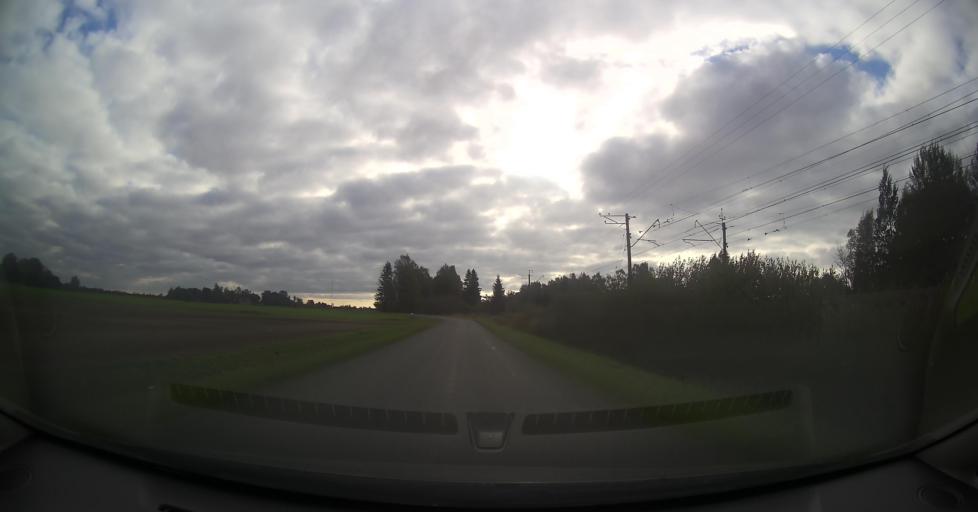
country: EE
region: Harju
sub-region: Anija vald
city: Kehra
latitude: 59.3514
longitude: 25.2869
